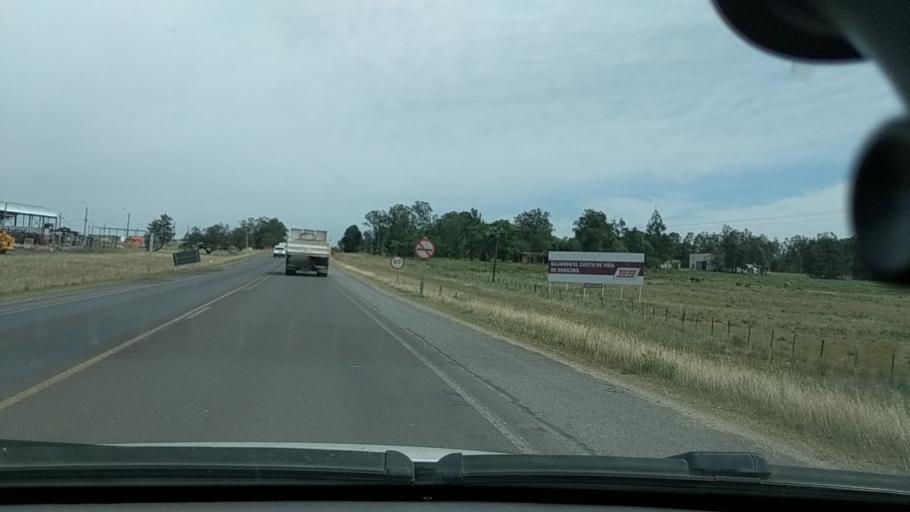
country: UY
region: Durazno
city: Durazno
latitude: -33.4211
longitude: -56.5032
